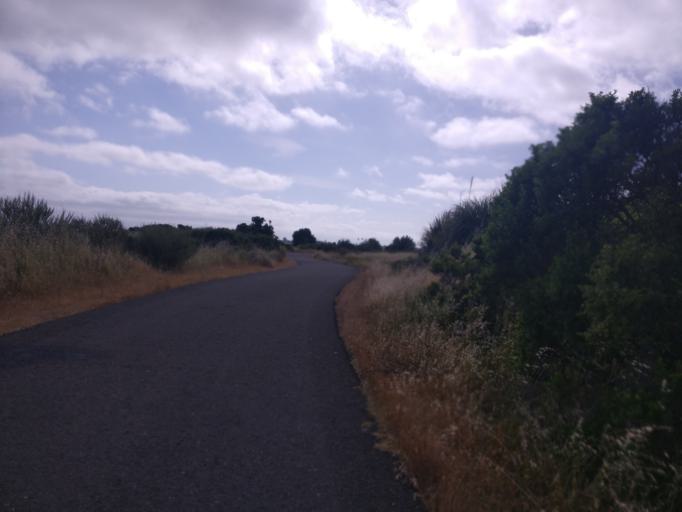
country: US
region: California
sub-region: Alameda County
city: Alameda
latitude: 37.7549
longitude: -122.2131
